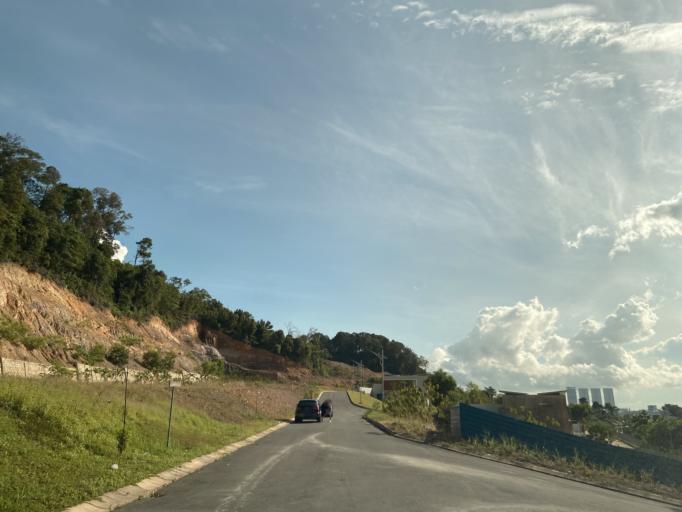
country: SG
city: Singapore
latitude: 1.0952
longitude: 104.0271
